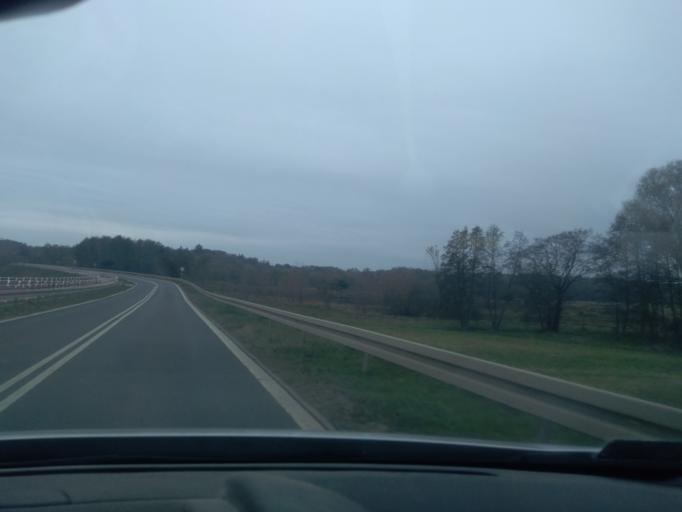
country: PL
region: Greater Poland Voivodeship
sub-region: Powiat poznanski
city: Murowana Goslina
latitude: 52.5415
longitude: 16.9638
